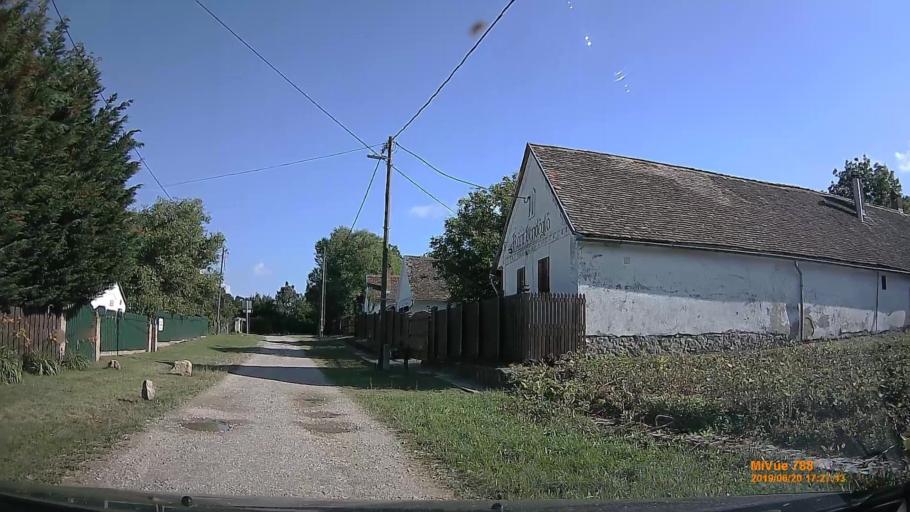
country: HU
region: Baranya
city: Buekkoesd
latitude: 46.1601
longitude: 18.0105
